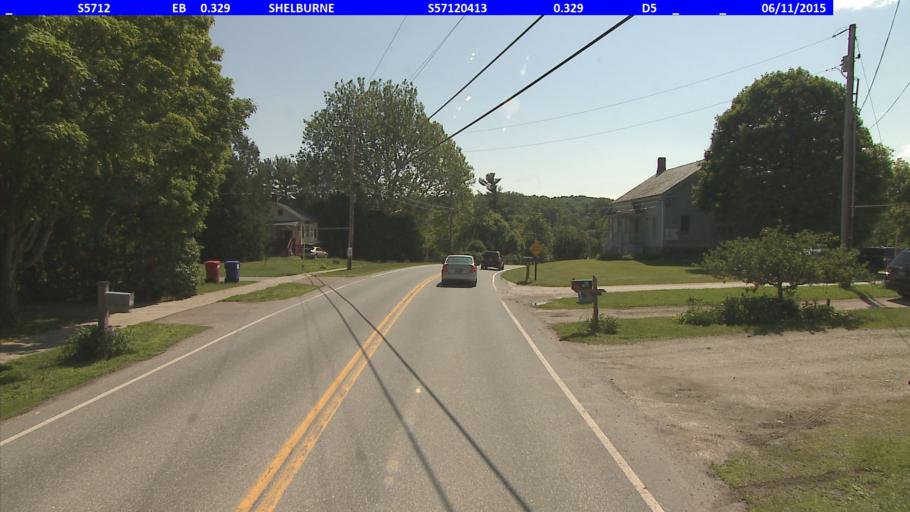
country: US
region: Vermont
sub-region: Chittenden County
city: Burlington
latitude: 44.3709
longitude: -73.2181
